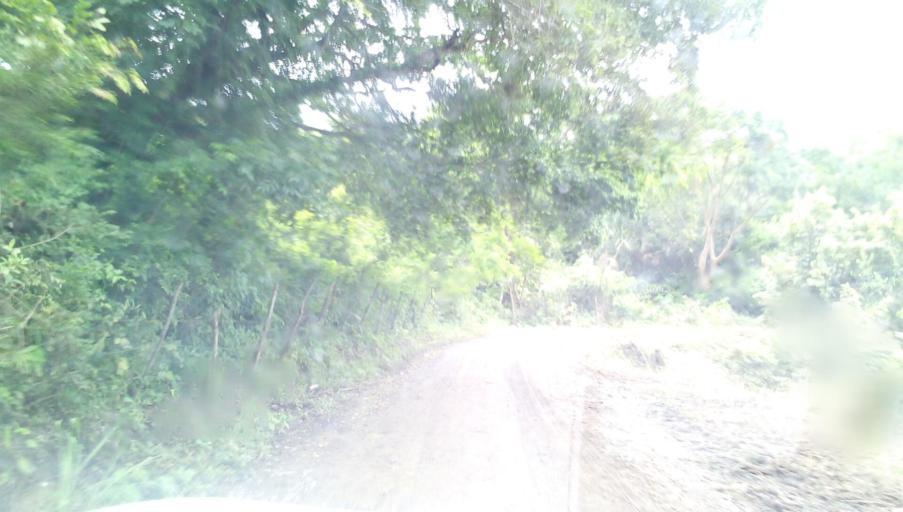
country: MX
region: Veracruz
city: Tepetzintla
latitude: 21.1397
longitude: -97.8516
